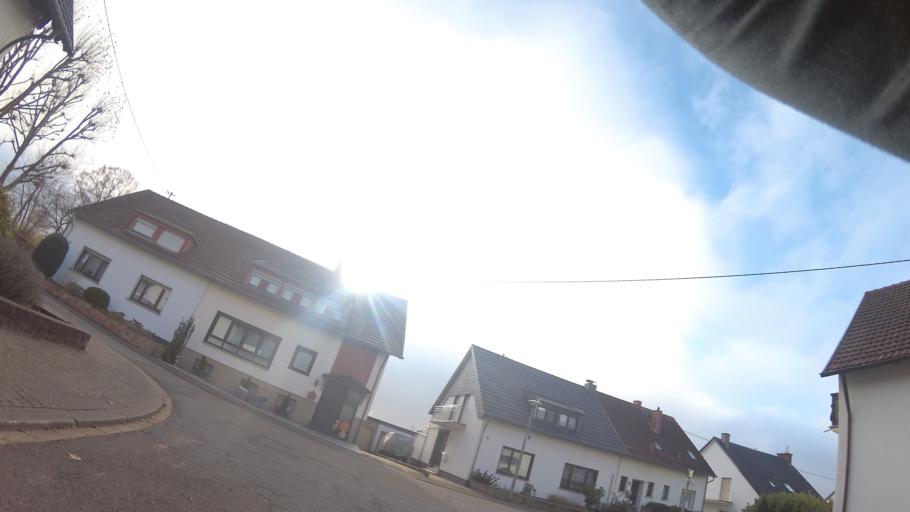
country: DE
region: Saarland
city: Ensdorf
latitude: 49.3016
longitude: 6.7834
